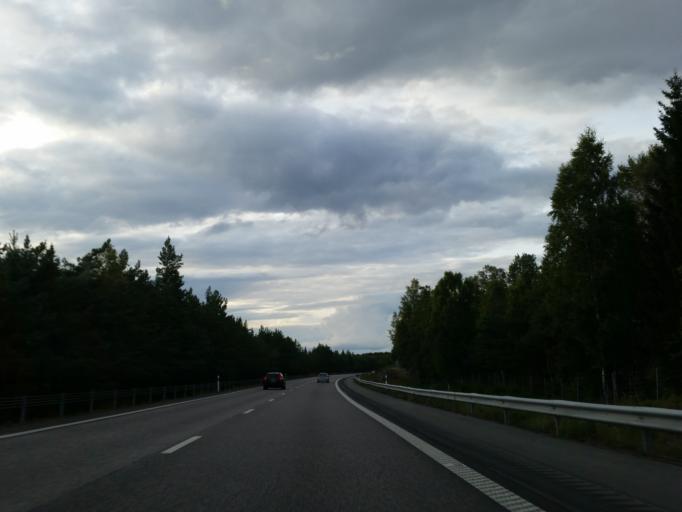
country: SE
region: Uppsala
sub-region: Knivsta Kommun
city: Knivsta
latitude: 59.7024
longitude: 17.8574
